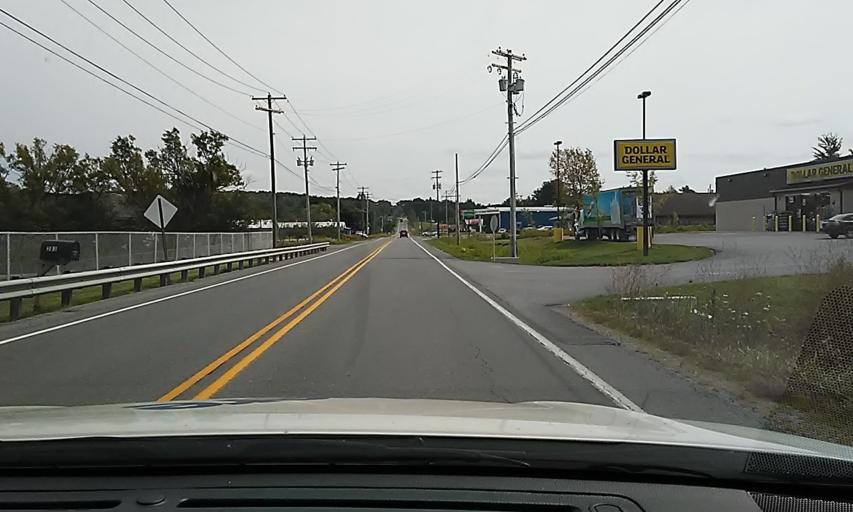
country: US
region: Pennsylvania
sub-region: Elk County
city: Saint Marys
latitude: 41.3618
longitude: -78.5920
